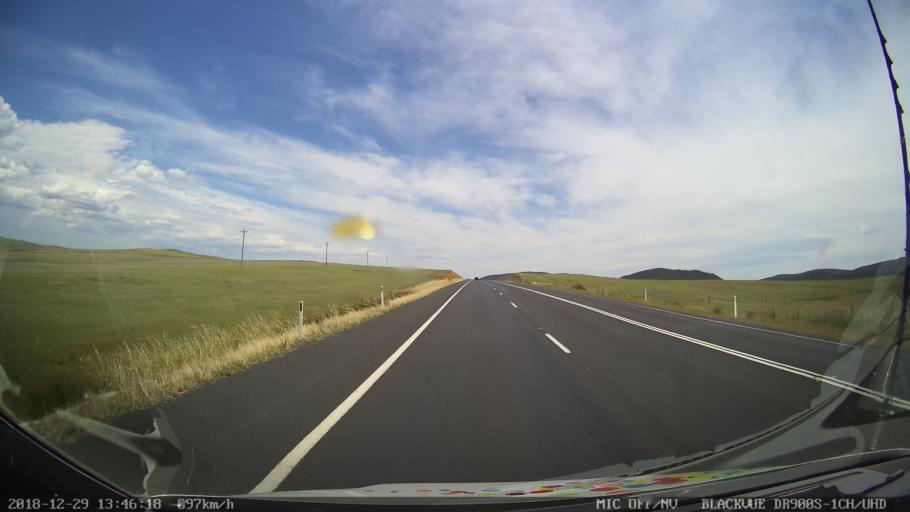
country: AU
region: New South Wales
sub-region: Cooma-Monaro
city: Cooma
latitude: -36.1095
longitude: 149.1431
